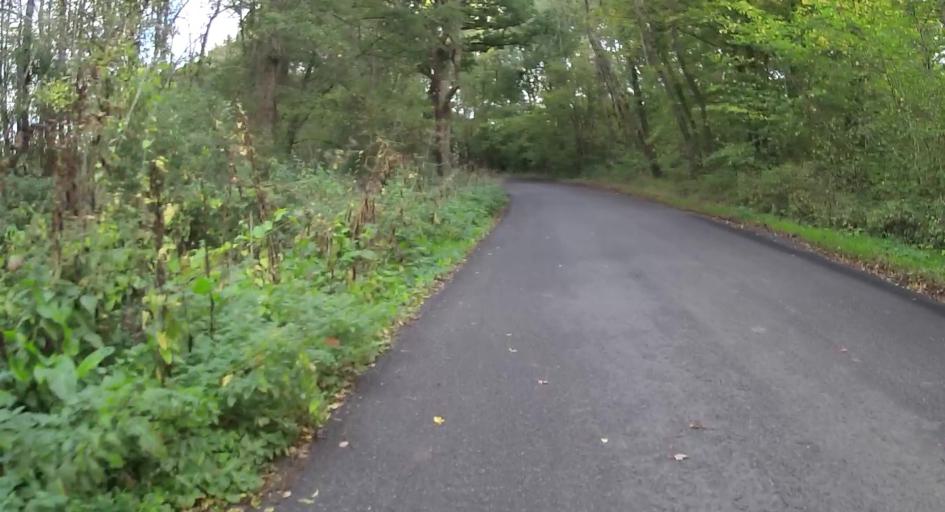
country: GB
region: England
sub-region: Hampshire
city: Odiham
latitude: 51.2749
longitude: -0.9042
